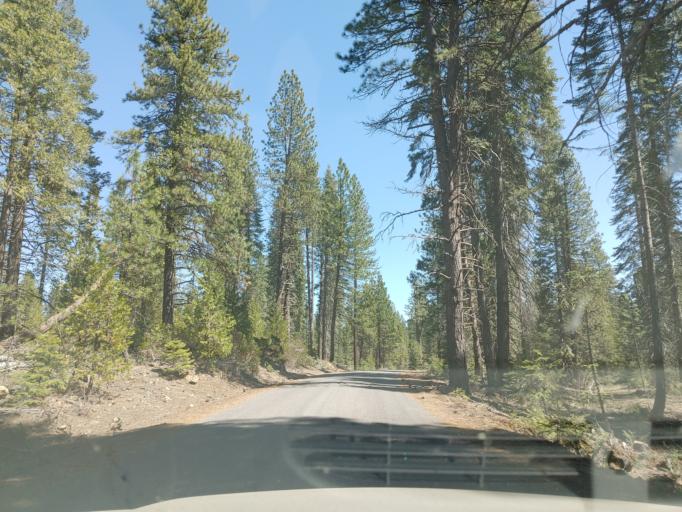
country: US
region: California
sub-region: Siskiyou County
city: McCloud
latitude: 41.2440
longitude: -121.9697
